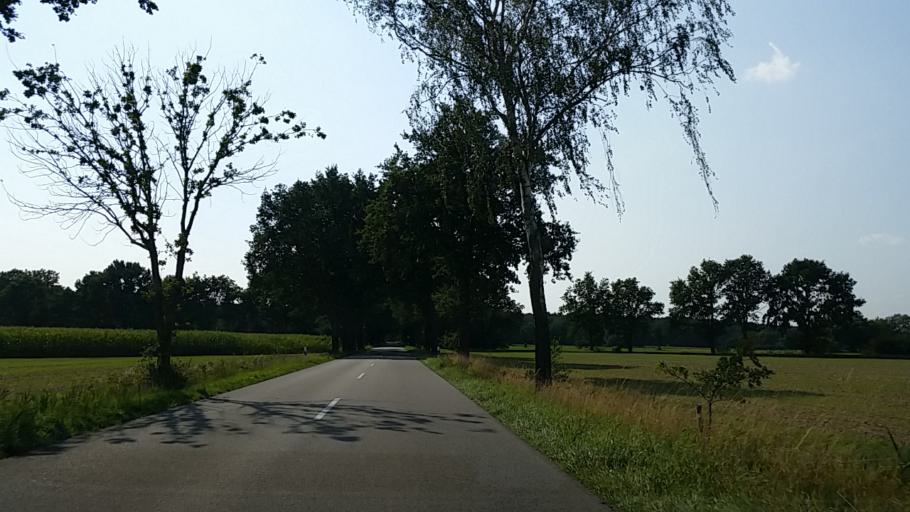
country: DE
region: Lower Saxony
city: Langendorf
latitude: 53.1141
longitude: 11.2335
